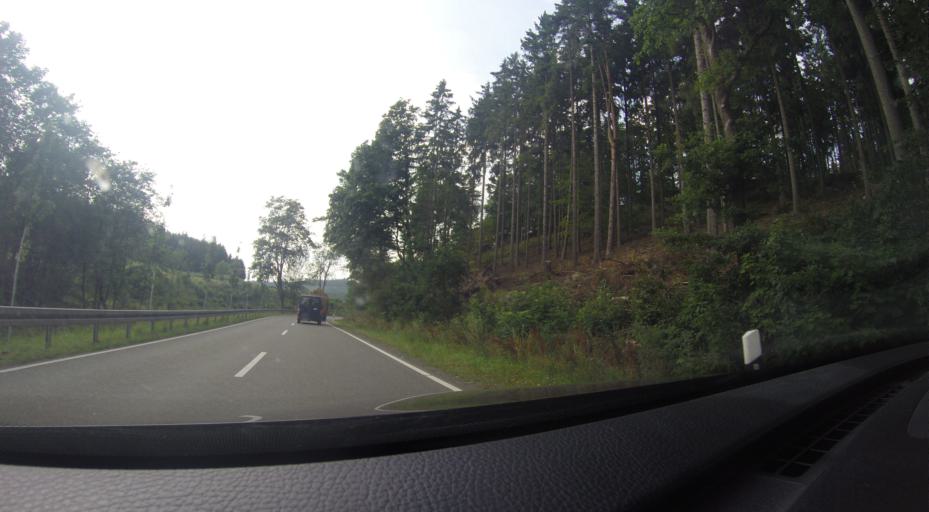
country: DE
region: North Rhine-Westphalia
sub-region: Regierungsbezirk Arnsberg
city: Medebach
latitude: 51.2120
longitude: 8.6706
